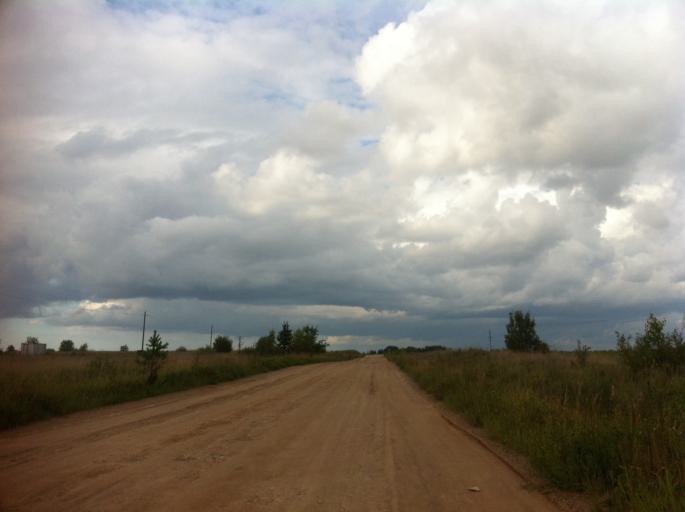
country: RU
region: Pskov
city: Izborsk
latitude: 57.8241
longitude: 27.9797
